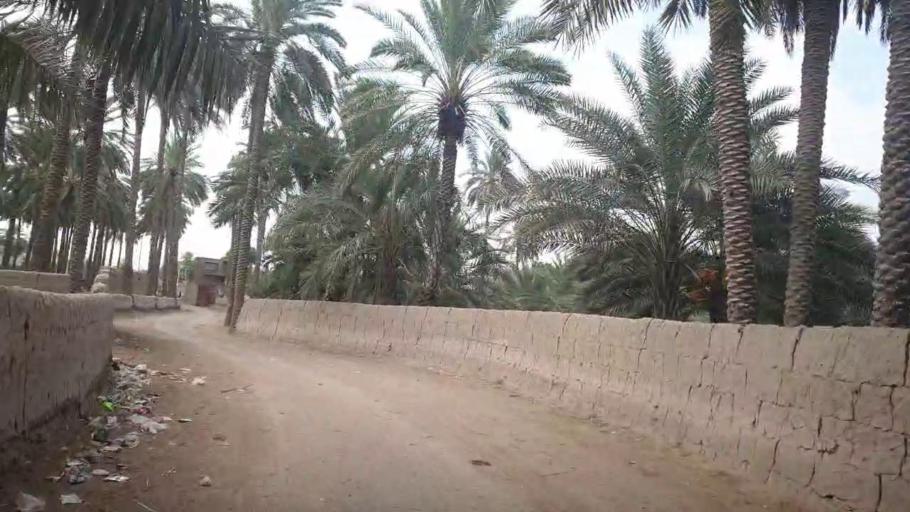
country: PK
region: Sindh
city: Sukkur
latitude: 27.6388
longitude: 68.7903
